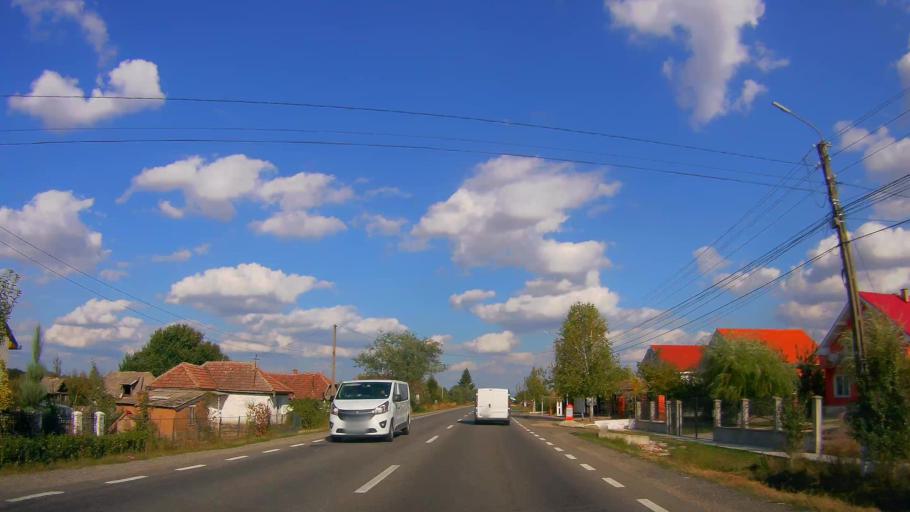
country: RO
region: Satu Mare
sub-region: Comuna Agris
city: Agris
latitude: 47.8708
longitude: 23.0190
